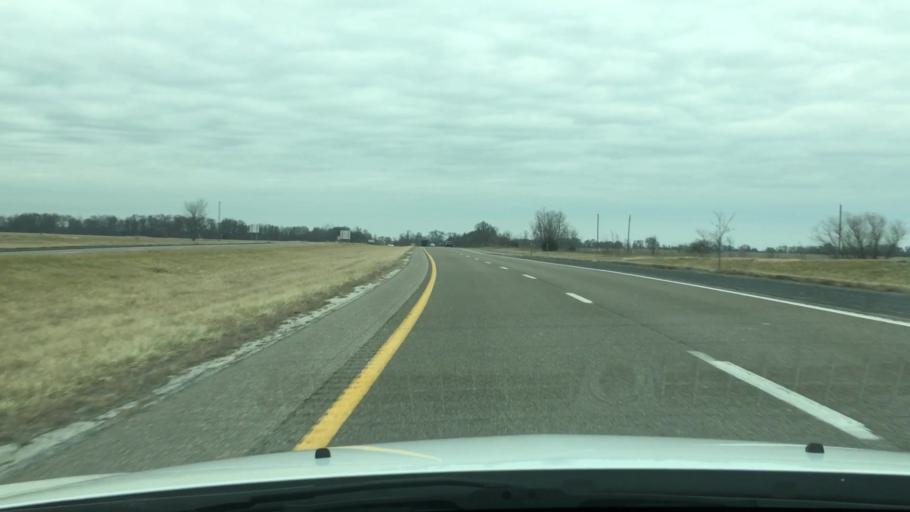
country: US
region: Missouri
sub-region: Audrain County
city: Mexico
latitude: 39.0196
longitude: -91.8859
